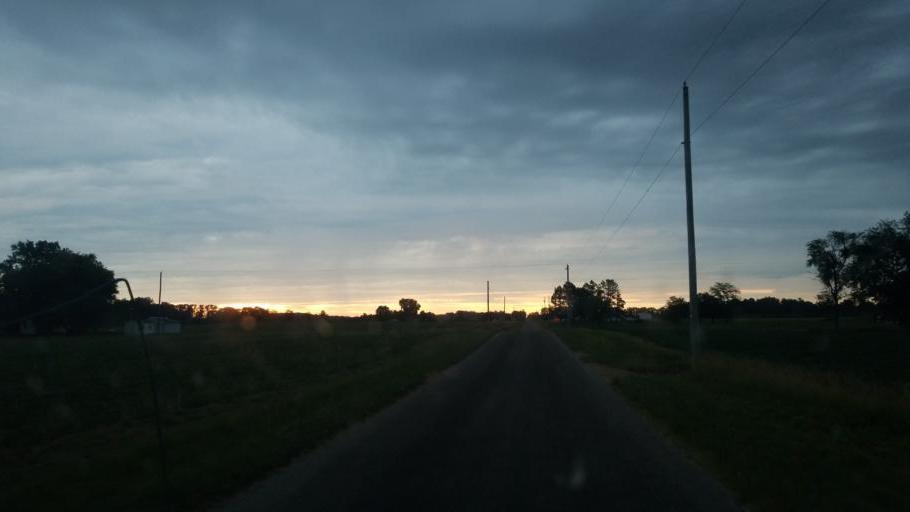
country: US
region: Ohio
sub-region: Defiance County
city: Hicksville
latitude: 41.3681
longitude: -84.7877
